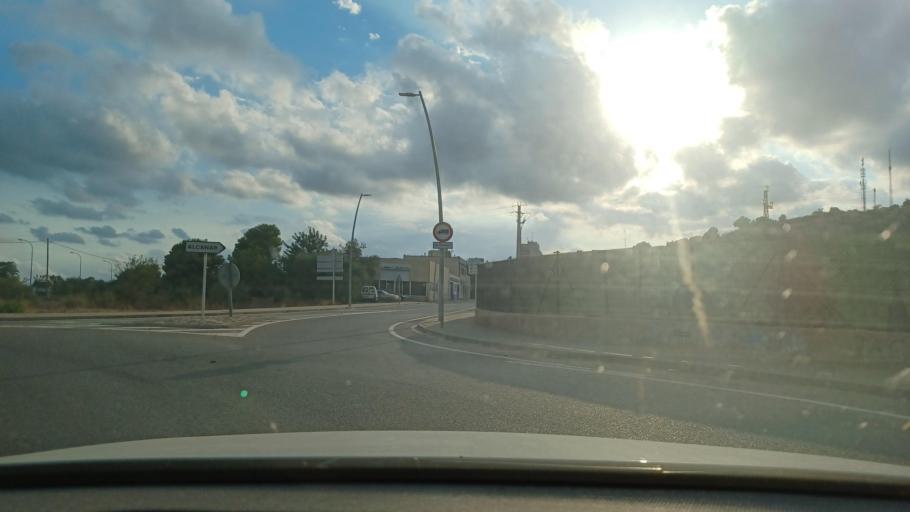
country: ES
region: Catalonia
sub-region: Provincia de Tarragona
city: Alcanar
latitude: 40.5445
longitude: 0.4900
